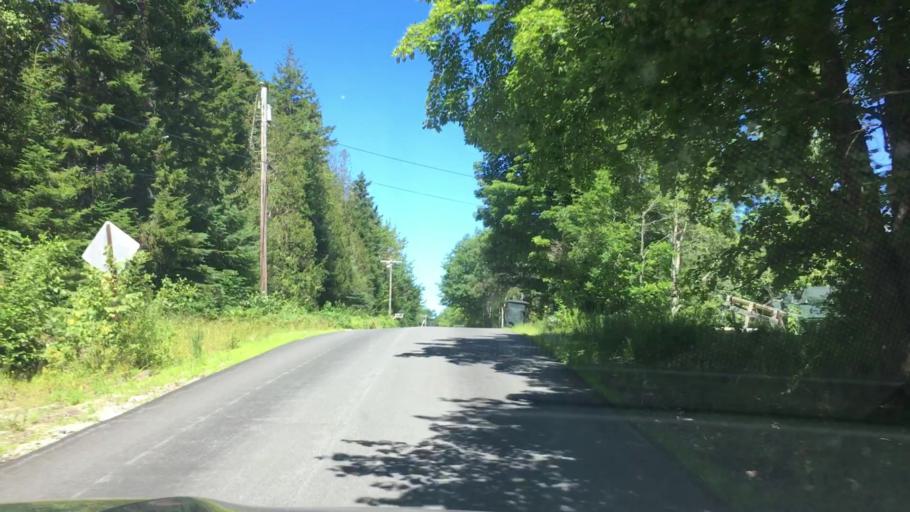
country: US
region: Maine
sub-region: Hancock County
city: Sedgwick
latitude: 44.3186
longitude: -68.6256
